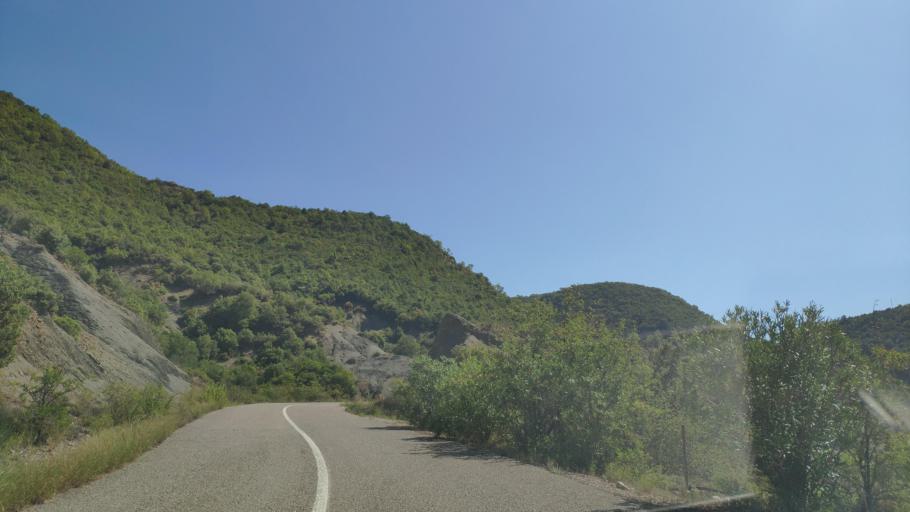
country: GR
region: Central Greece
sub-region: Nomos Evrytanias
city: Kerasochori
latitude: 39.0071
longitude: 21.5277
